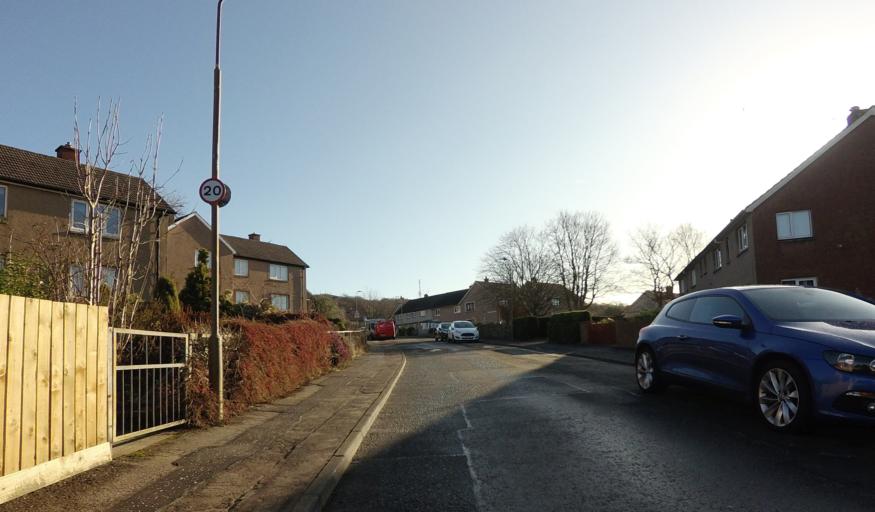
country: GB
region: Scotland
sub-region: Edinburgh
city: Colinton
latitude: 55.9536
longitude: -3.2831
